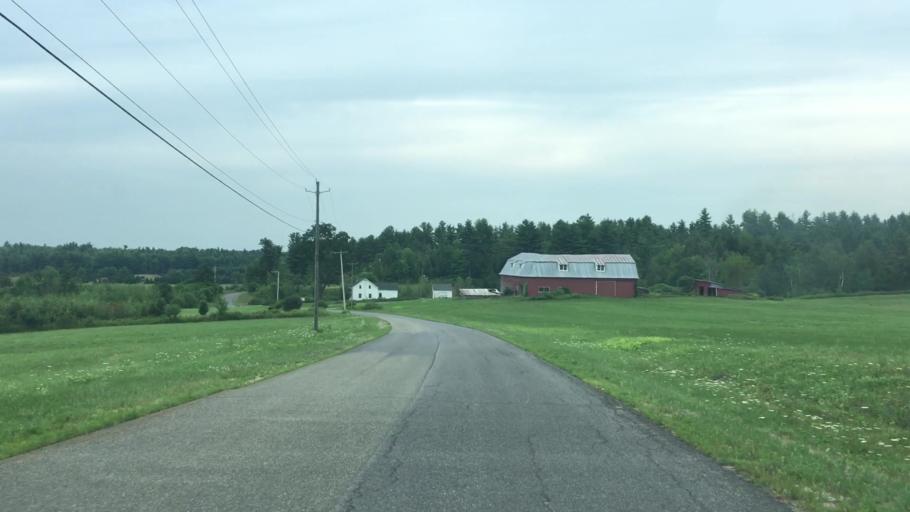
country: US
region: New York
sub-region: Clinton County
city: Peru
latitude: 44.6040
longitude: -73.6179
